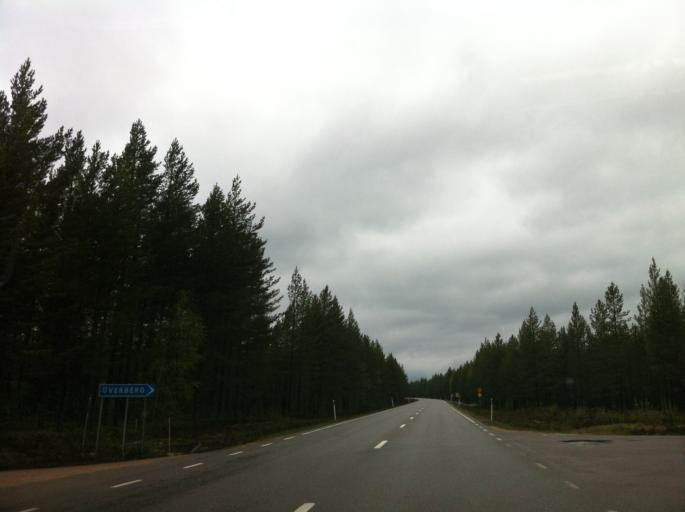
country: SE
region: Jaemtland
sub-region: Harjedalens Kommun
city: Sveg
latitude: 62.0556
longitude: 14.3015
